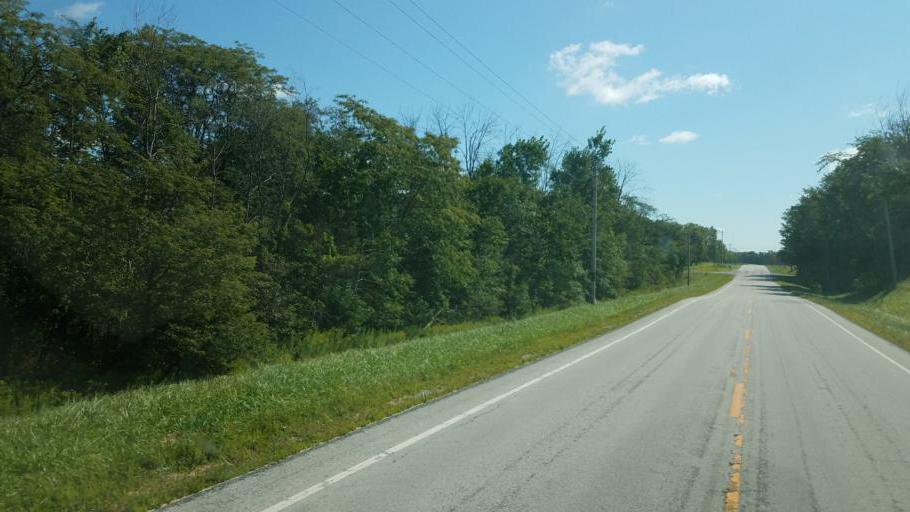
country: US
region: Ohio
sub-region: Wyandot County
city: Carey
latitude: 40.9477
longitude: -83.3360
